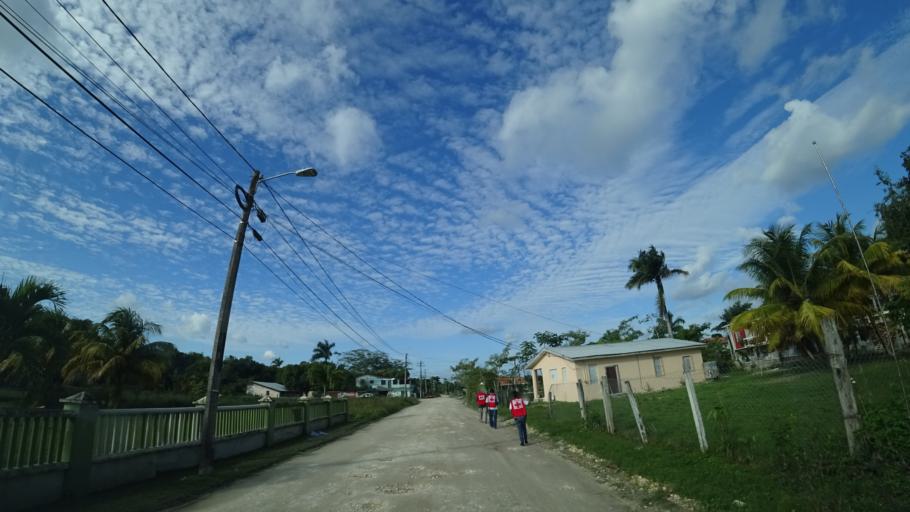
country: BZ
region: Belize
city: Belize City
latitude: 17.5678
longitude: -88.4086
